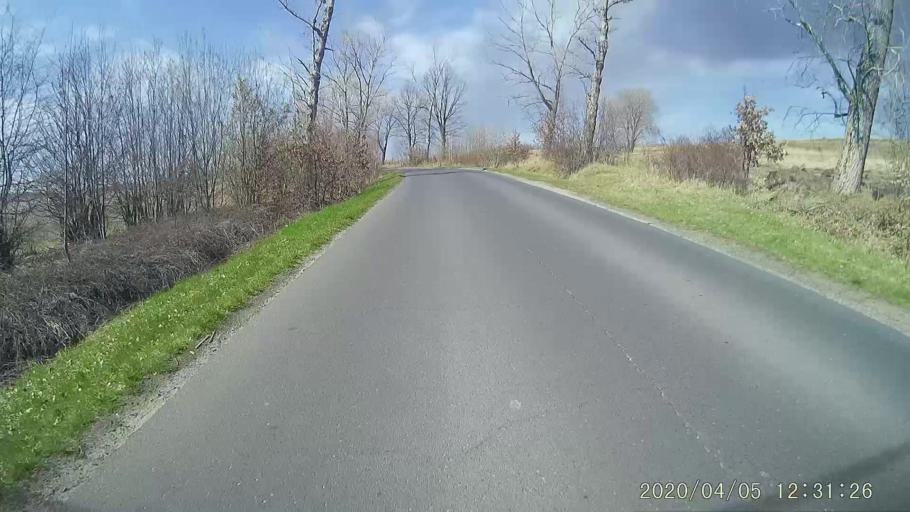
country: PL
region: Lower Silesian Voivodeship
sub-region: Powiat lwowecki
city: Mirsk
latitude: 51.0103
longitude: 15.3597
